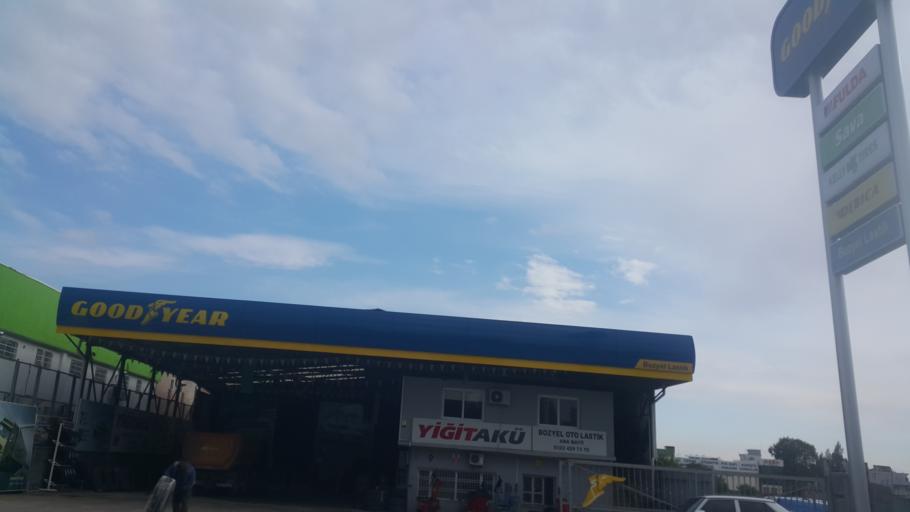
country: TR
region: Adana
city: Seyhan
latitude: 36.9972
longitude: 35.2439
